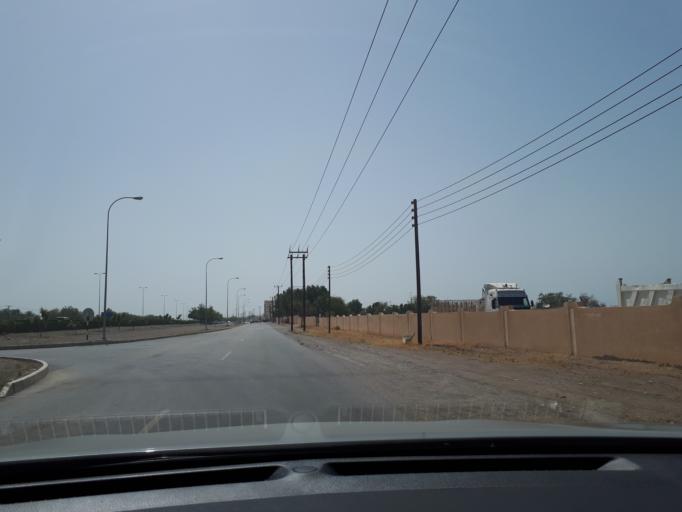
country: OM
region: Muhafazat Masqat
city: As Sib al Jadidah
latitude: 23.6939
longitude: 58.0628
